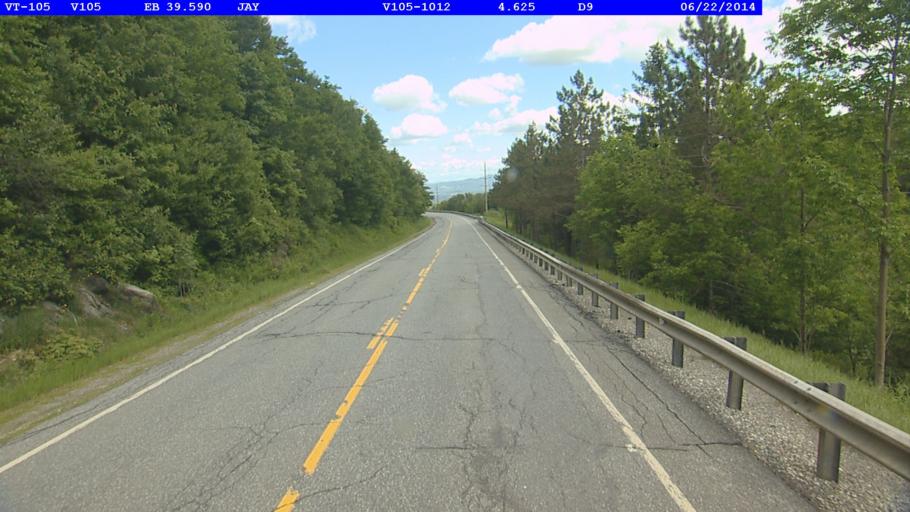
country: CA
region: Quebec
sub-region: Monteregie
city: Sutton
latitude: 44.9833
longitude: -72.4914
